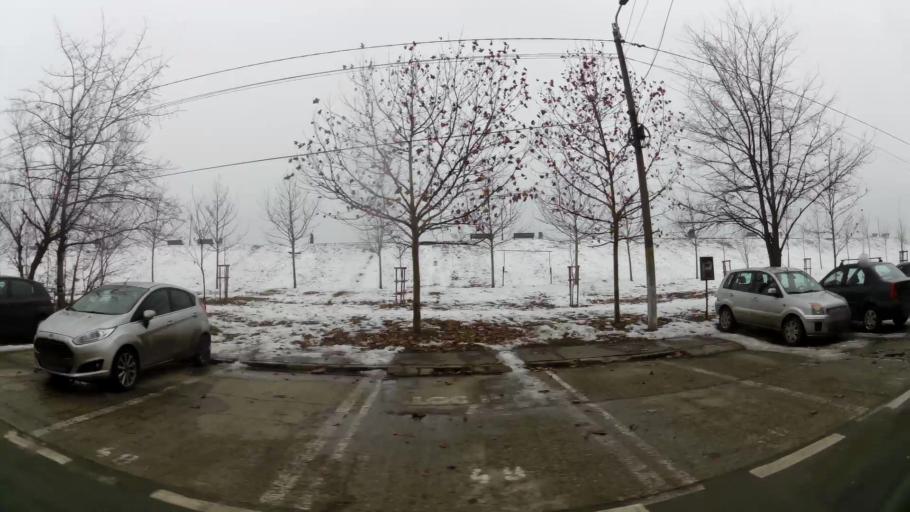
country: RO
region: Ilfov
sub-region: Comuna Chiajna
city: Rosu
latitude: 44.4537
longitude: 26.0393
